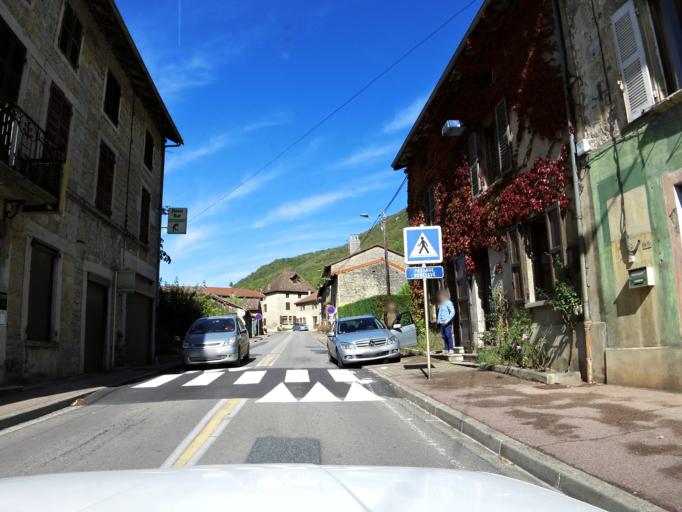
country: FR
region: Rhone-Alpes
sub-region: Departement de l'Ain
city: Saint-Sorlin-en-Bugey
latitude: 45.8857
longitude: 5.3709
